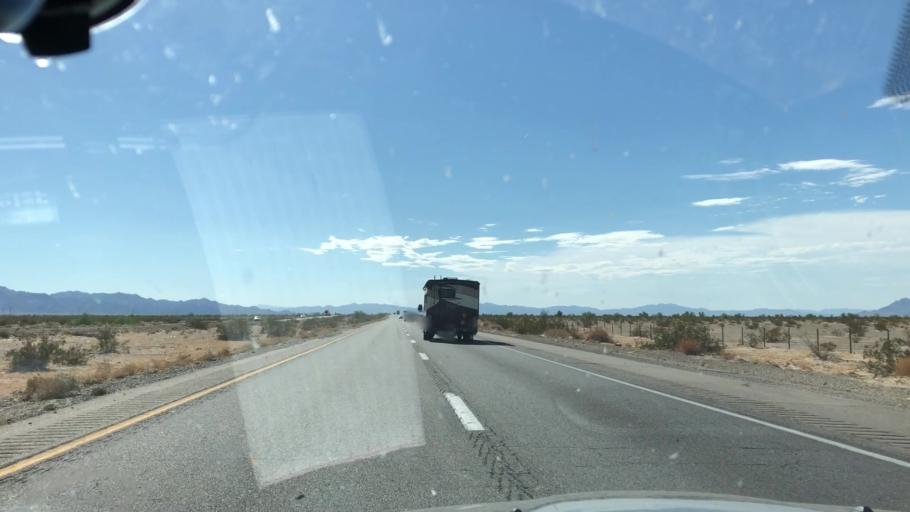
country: US
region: California
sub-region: Riverside County
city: Mesa Verde
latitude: 33.6493
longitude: -115.1308
